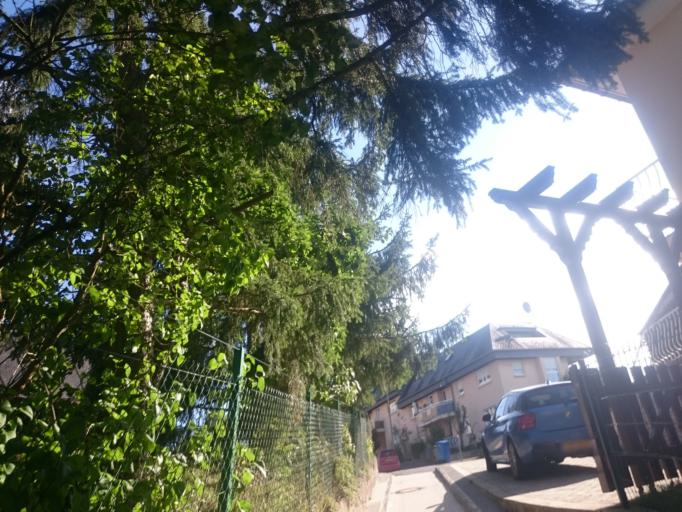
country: LU
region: Luxembourg
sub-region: Canton de Luxembourg
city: Luxembourg
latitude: 49.5864
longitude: 6.1042
